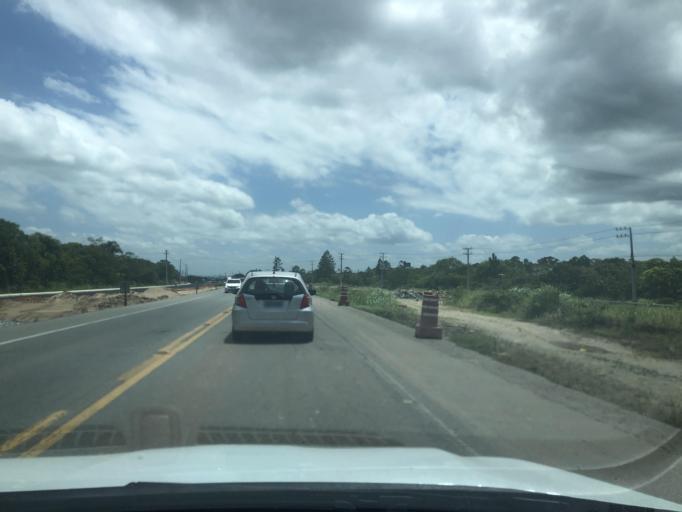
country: BR
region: Santa Catarina
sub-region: Joinville
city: Joinville
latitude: -26.3906
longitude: -48.7352
